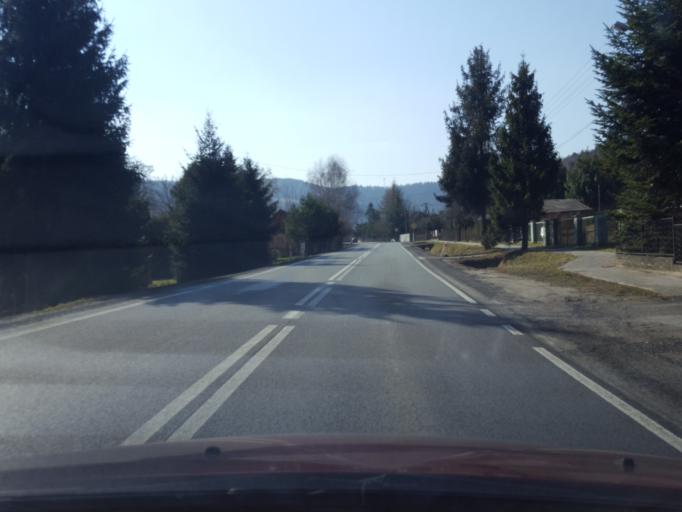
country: PL
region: Lesser Poland Voivodeship
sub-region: Powiat brzeski
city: Czchow
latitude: 49.8189
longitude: 20.6813
